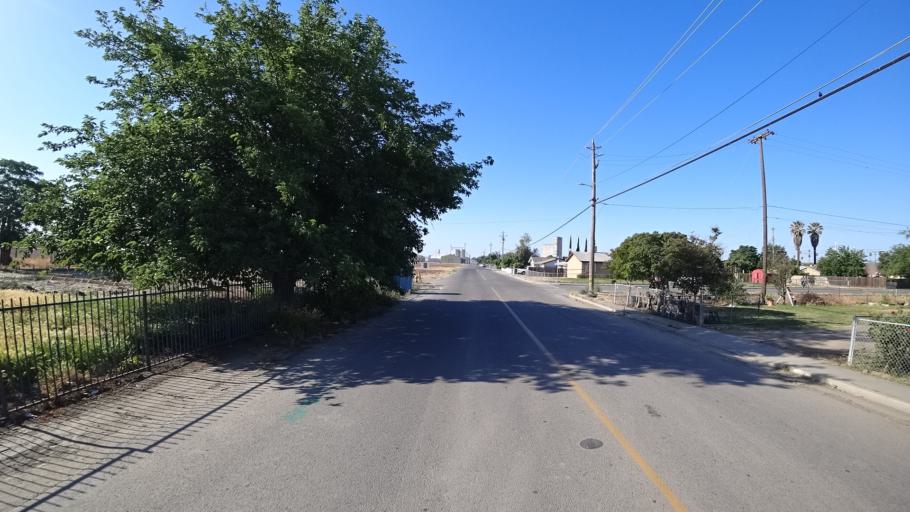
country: US
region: California
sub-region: Kings County
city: Corcoran
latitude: 36.1018
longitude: -119.5542
